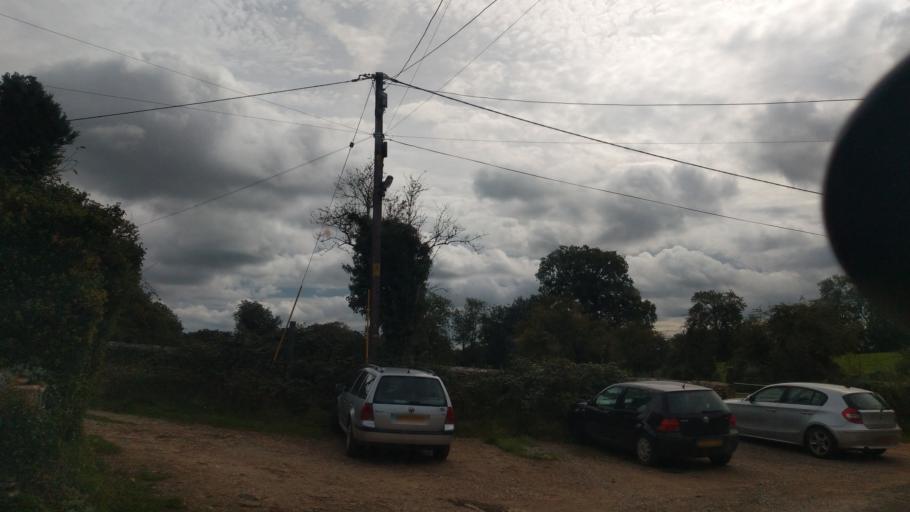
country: GB
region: England
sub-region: Wiltshire
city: Corsham
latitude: 51.4335
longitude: -2.1652
